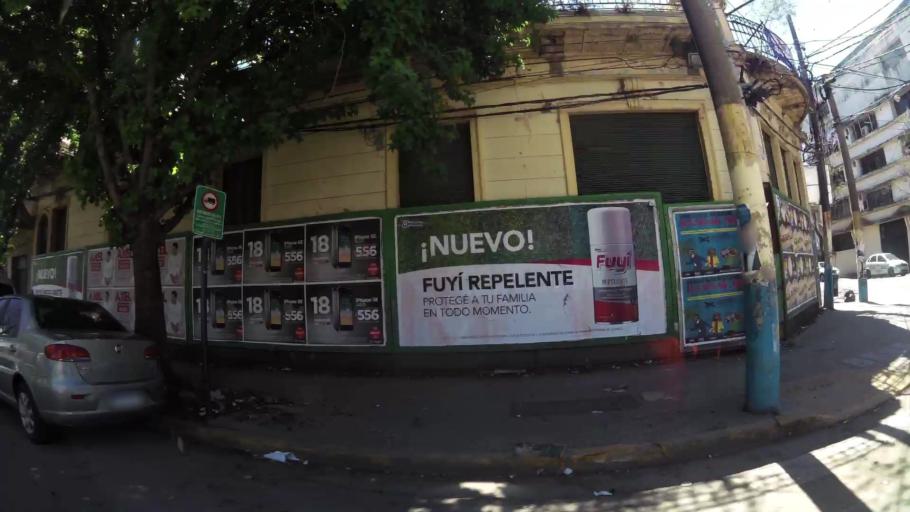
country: AR
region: Santa Fe
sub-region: Departamento de Rosario
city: Rosario
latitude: -32.9337
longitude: -60.6693
